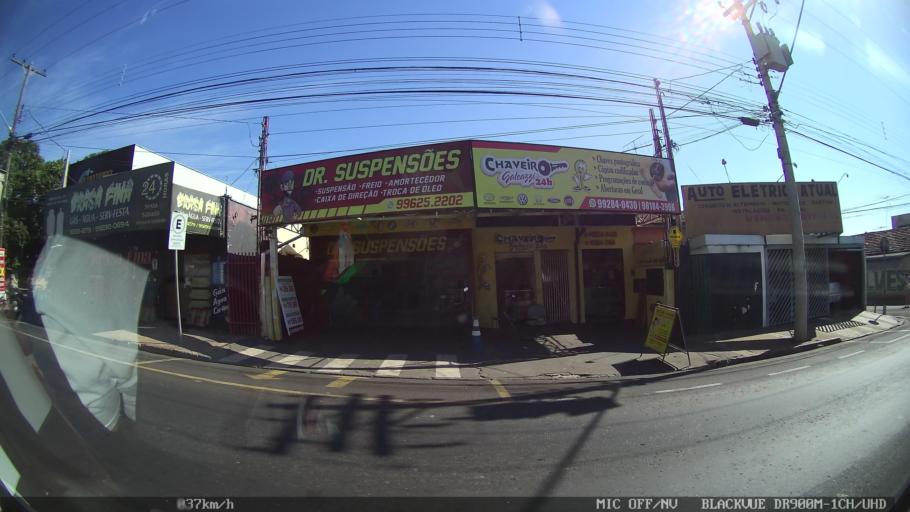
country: BR
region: Sao Paulo
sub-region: Sao Jose Do Rio Preto
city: Sao Jose do Rio Preto
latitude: -20.7734
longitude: -49.3638
